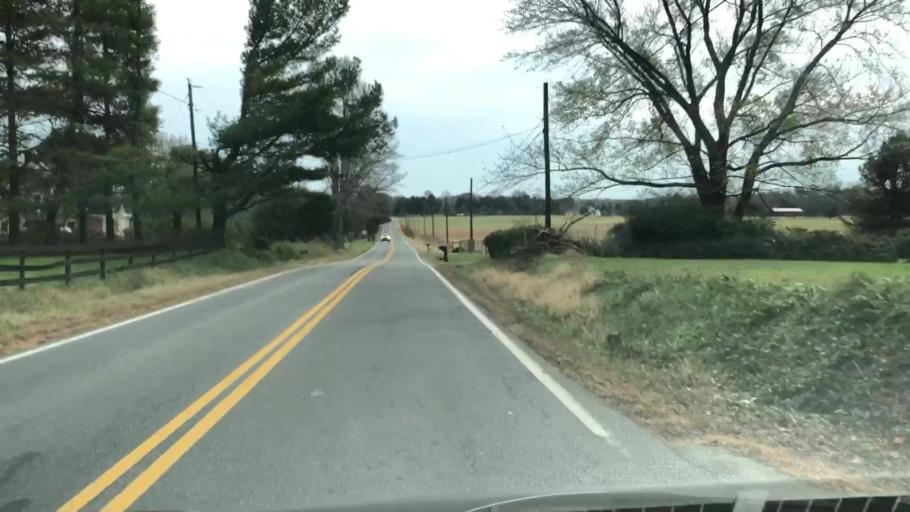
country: US
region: Virginia
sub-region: Fauquier County
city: New Baltimore
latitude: 38.7622
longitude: -77.6797
